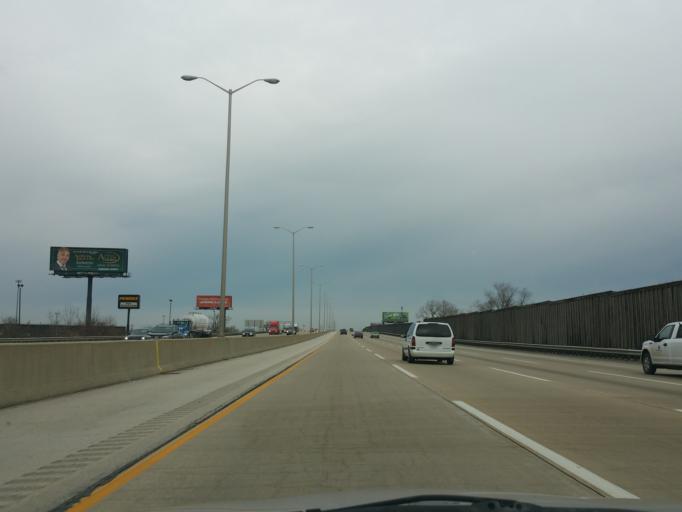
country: US
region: Illinois
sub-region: Cook County
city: Chicago Ridge
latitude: 41.7078
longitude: -87.7941
